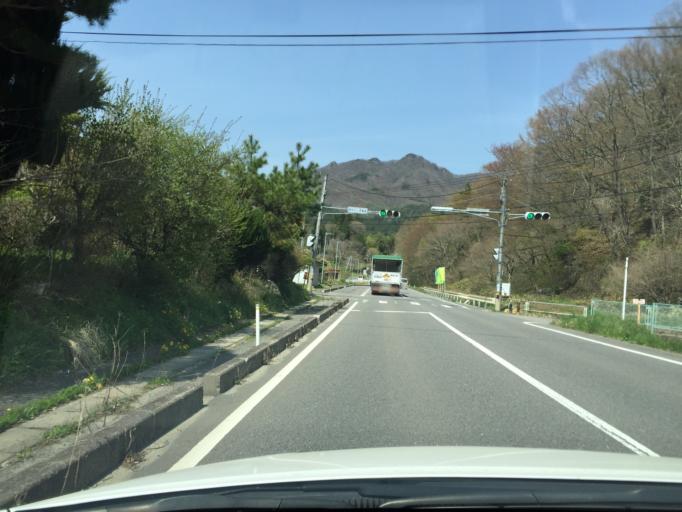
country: JP
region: Fukushima
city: Funehikimachi-funehiki
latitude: 37.4508
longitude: 140.6781
